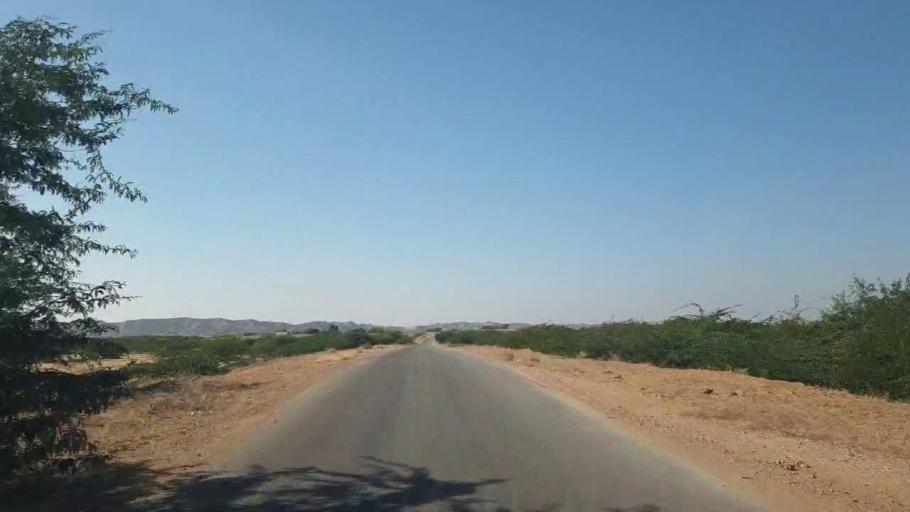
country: PK
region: Sindh
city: Malir Cantonment
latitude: 25.2834
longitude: 67.5799
